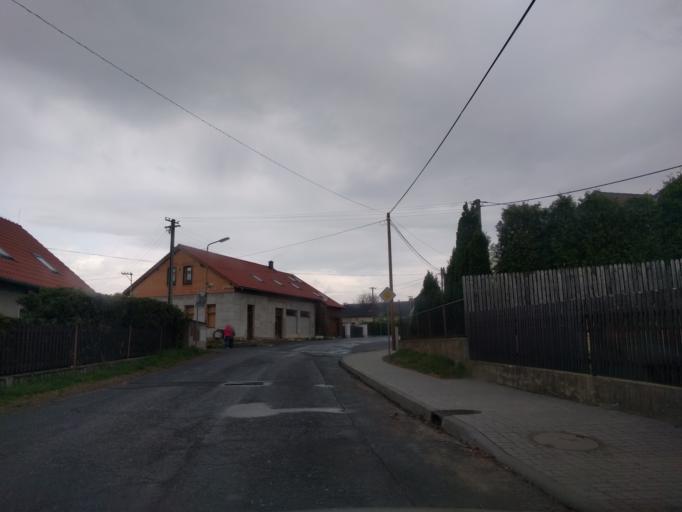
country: CZ
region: Central Bohemia
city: Dobris
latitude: 49.7030
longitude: 14.1433
